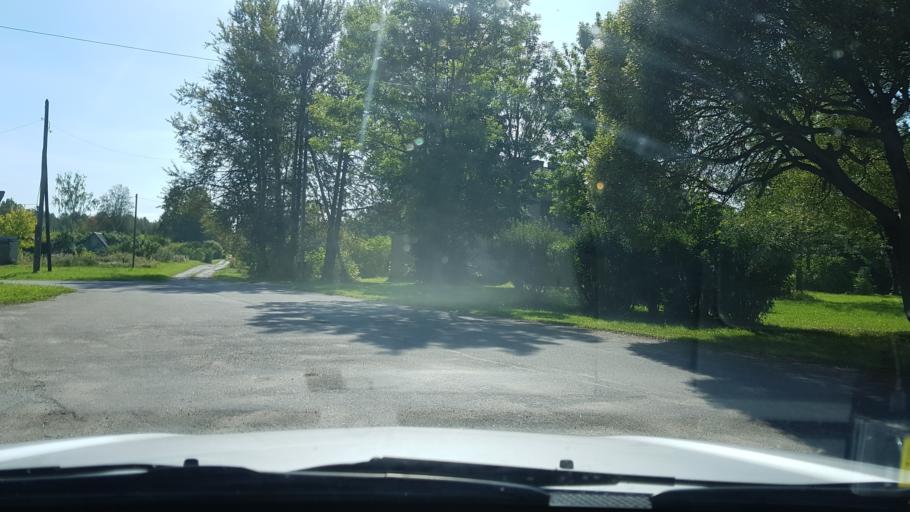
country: EE
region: Ida-Virumaa
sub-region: Sillamaee linn
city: Sillamae
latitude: 59.3201
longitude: 27.7812
